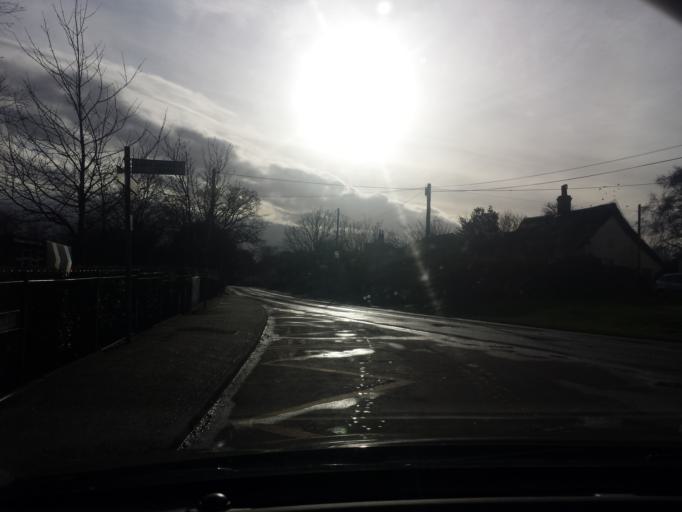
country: GB
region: England
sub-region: Essex
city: Alresford
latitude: 51.8952
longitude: 1.0271
